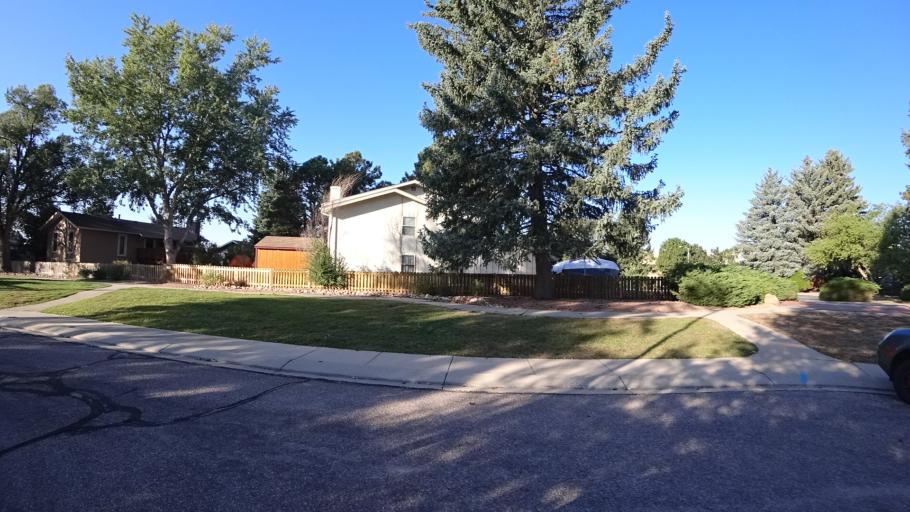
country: US
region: Colorado
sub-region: El Paso County
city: Cimarron Hills
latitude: 38.8782
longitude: -104.7528
